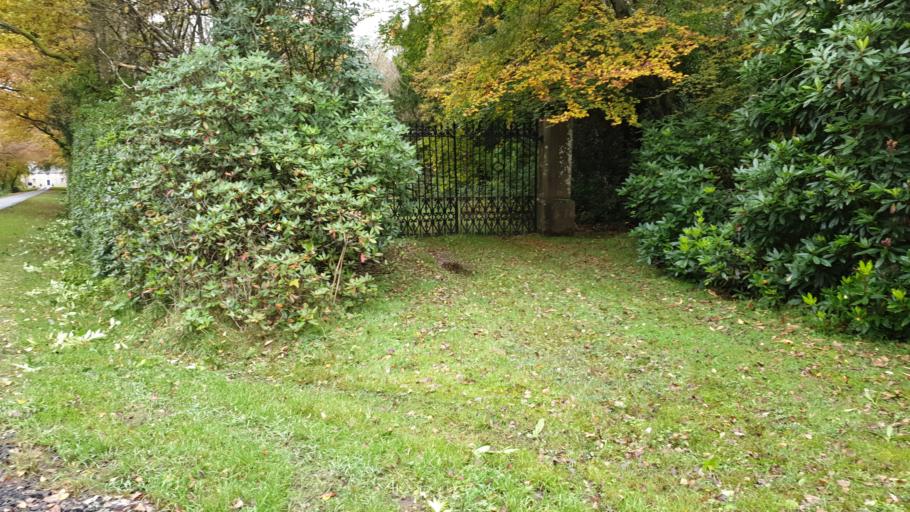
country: GB
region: Scotland
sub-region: East Ayrshire
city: Catrine
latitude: 55.4757
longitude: -4.3607
